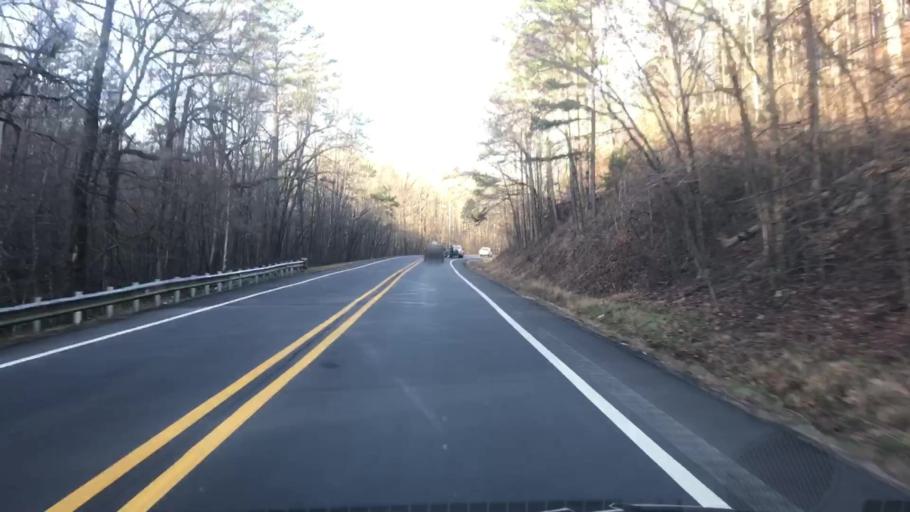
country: US
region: Arkansas
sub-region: Montgomery County
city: Mount Ida
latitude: 34.5235
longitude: -93.4091
